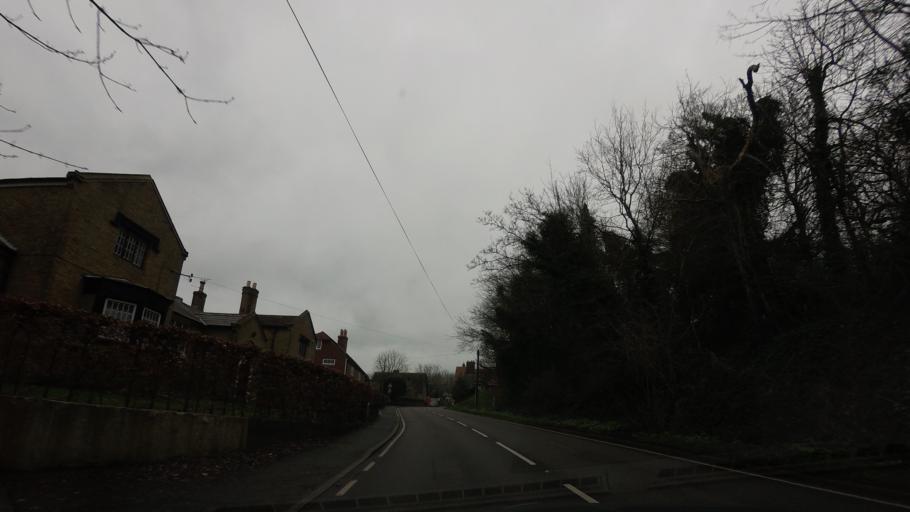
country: GB
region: England
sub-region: Kent
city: Maidstone
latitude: 51.2225
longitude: 0.5113
